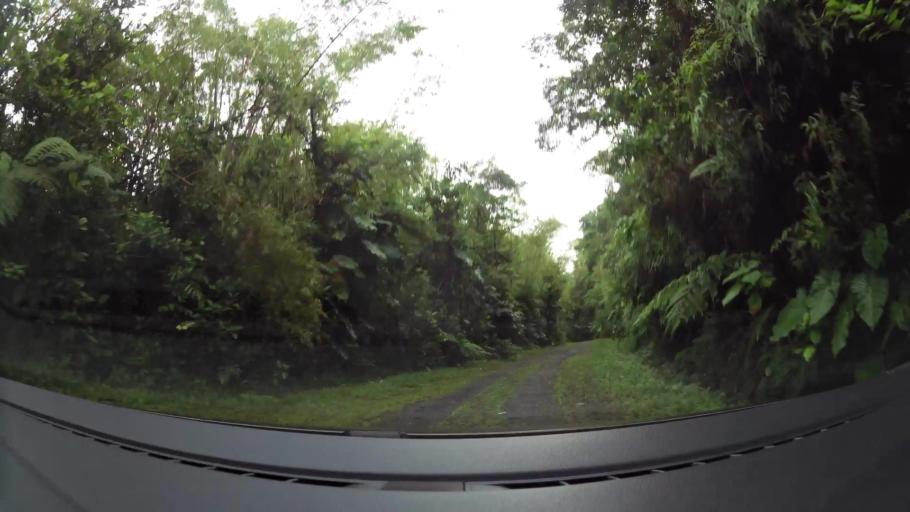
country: GP
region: Guadeloupe
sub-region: Guadeloupe
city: Trois-Rivieres
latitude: 16.0363
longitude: -61.6359
